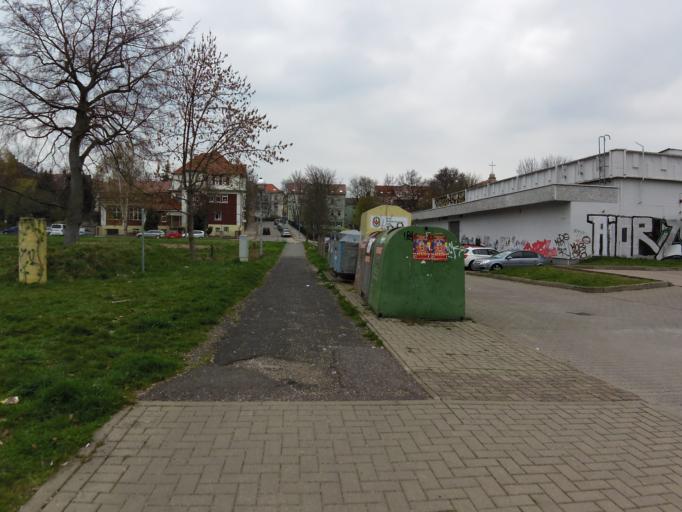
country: DE
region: Thuringia
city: Gotha
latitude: 50.9511
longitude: 10.7019
